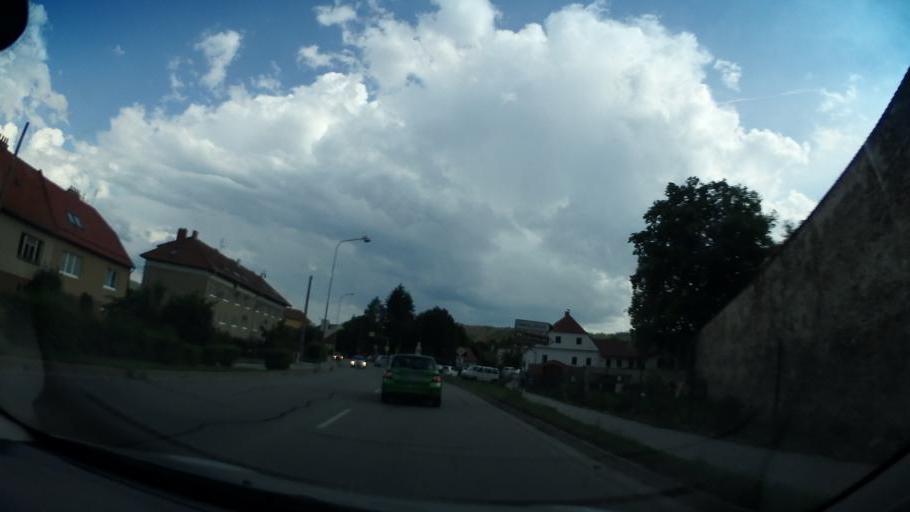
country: CZ
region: South Moravian
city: Predklasteri
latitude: 49.3551
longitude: 16.4018
